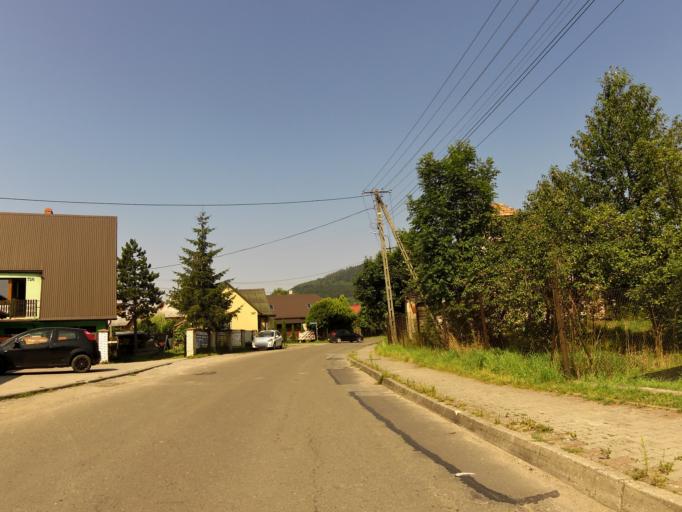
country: PL
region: Silesian Voivodeship
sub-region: Powiat zywiecki
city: Wieprz
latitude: 49.6458
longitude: 19.1787
